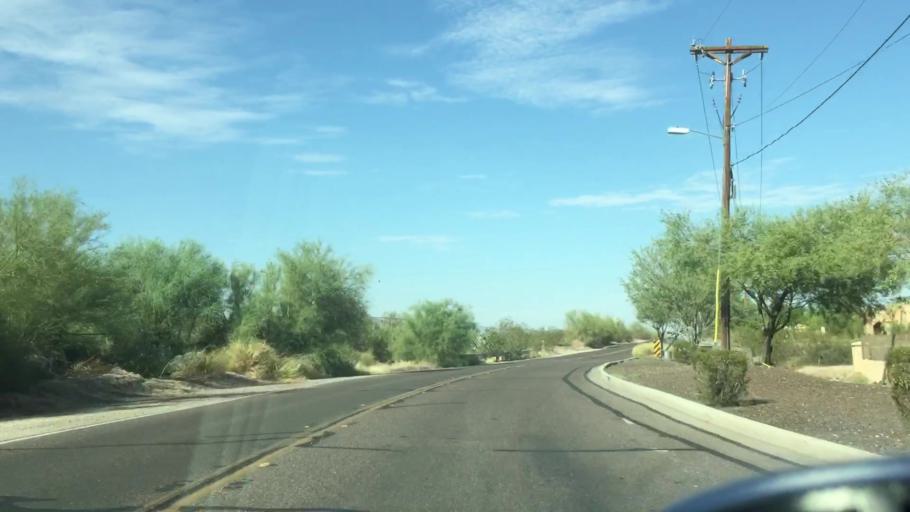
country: US
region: Arizona
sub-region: Maricopa County
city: Guadalupe
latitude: 33.3633
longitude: -112.0425
